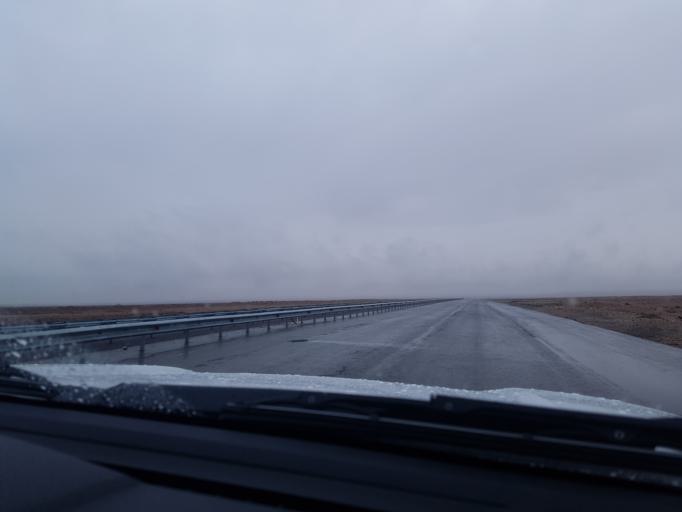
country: TM
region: Balkan
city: Turkmenbasy
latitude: 40.0272
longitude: 53.6705
